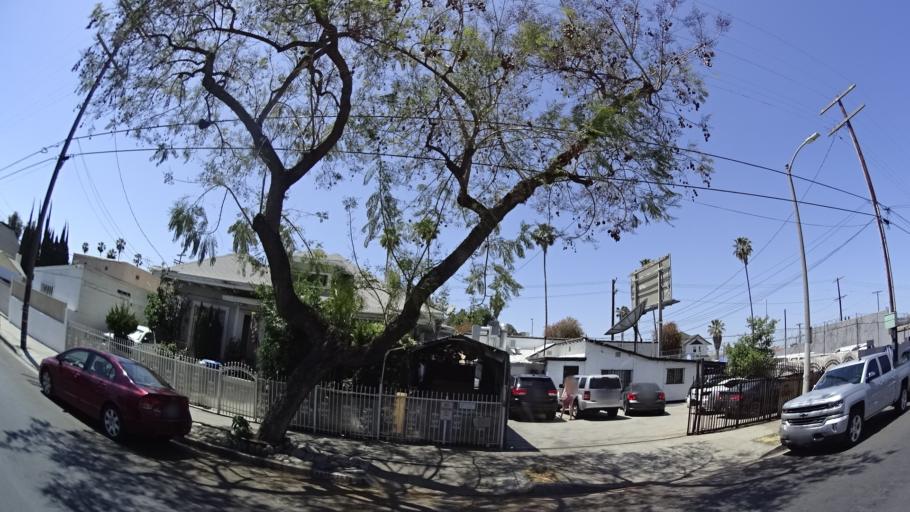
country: US
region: California
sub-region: Los Angeles County
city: Los Angeles
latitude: 34.0786
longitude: -118.2145
